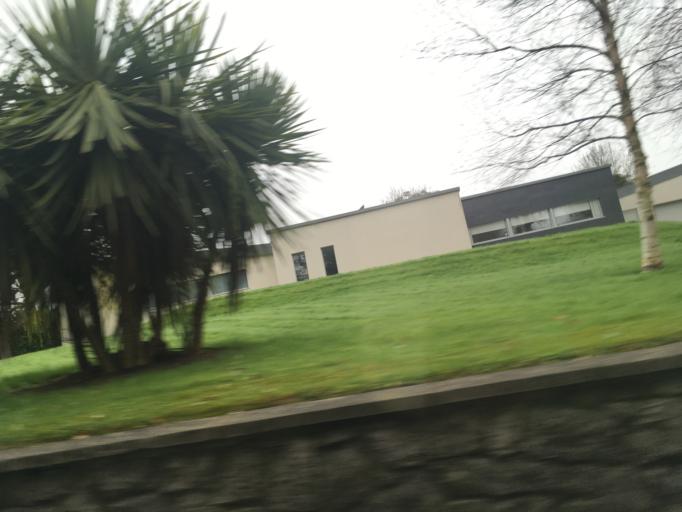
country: IE
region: Leinster
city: Portmarnock
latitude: 53.4303
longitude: -6.1522
